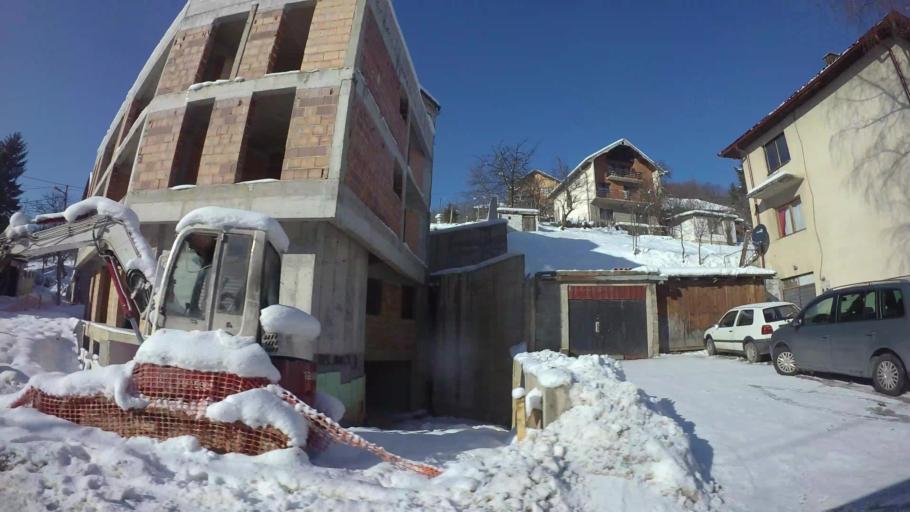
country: BA
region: Federation of Bosnia and Herzegovina
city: Kobilja Glava
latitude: 43.8843
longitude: 18.4156
